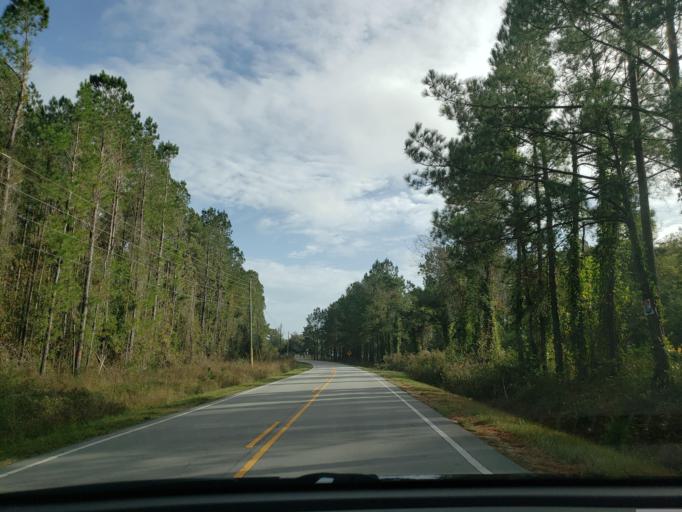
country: US
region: North Carolina
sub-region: Onslow County
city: Jacksonville
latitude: 34.6727
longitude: -77.4997
